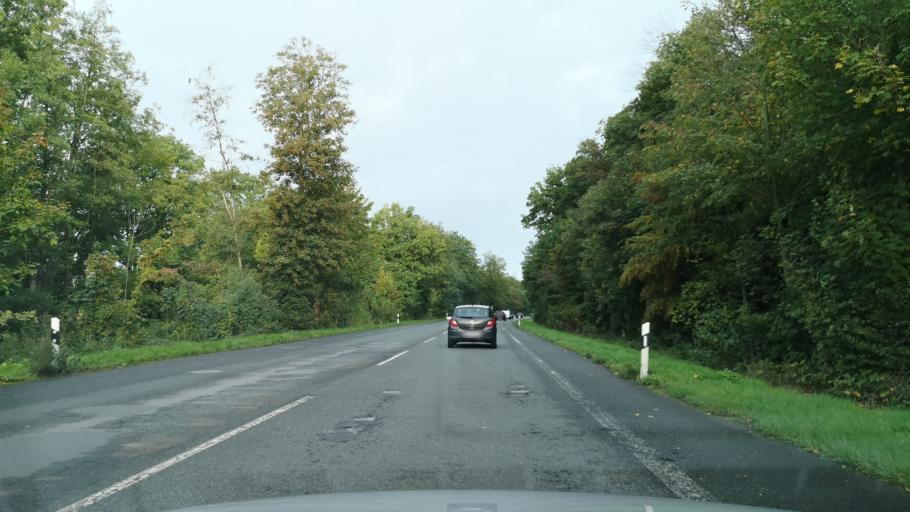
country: DE
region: North Rhine-Westphalia
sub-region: Regierungsbezirk Arnsberg
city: Hagen
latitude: 51.3977
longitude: 7.5058
